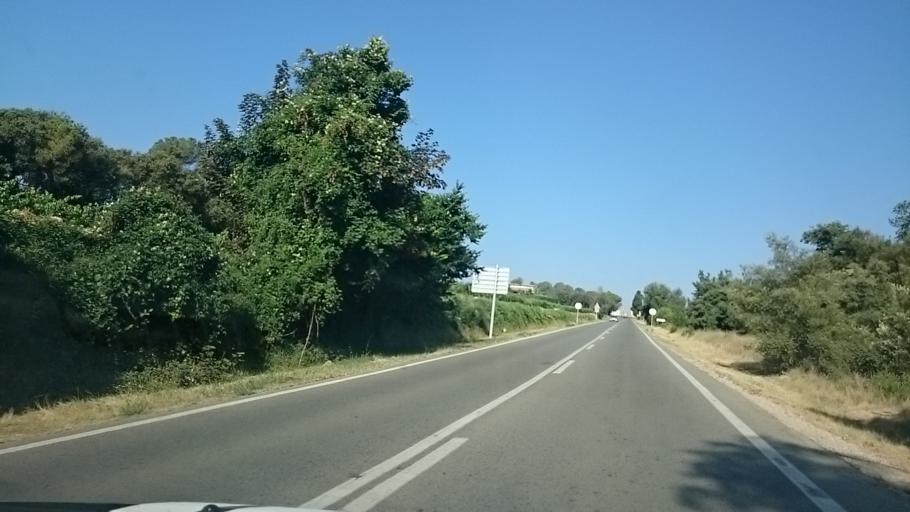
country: ES
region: Catalonia
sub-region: Provincia de Barcelona
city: Sant Marti Sarroca
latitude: 41.3844
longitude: 1.6326
